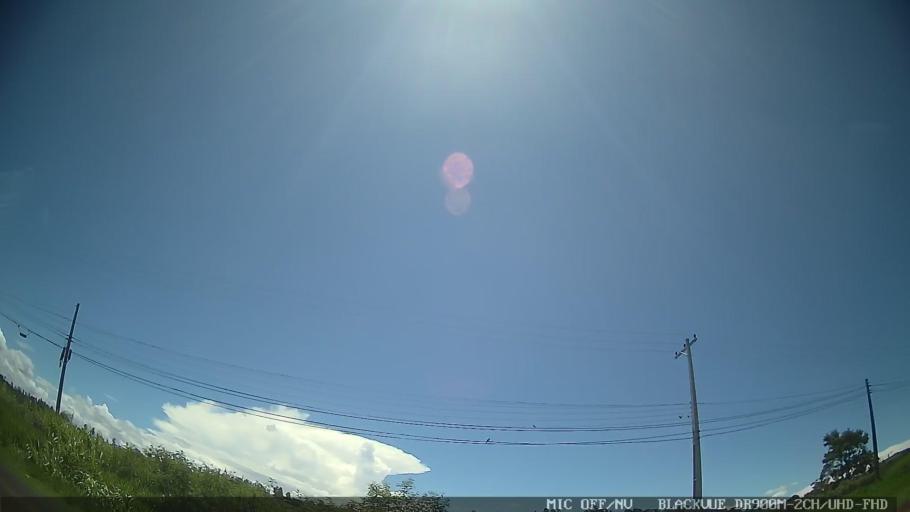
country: BR
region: Sao Paulo
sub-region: Pedreira
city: Pedreira
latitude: -22.7251
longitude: -46.9343
